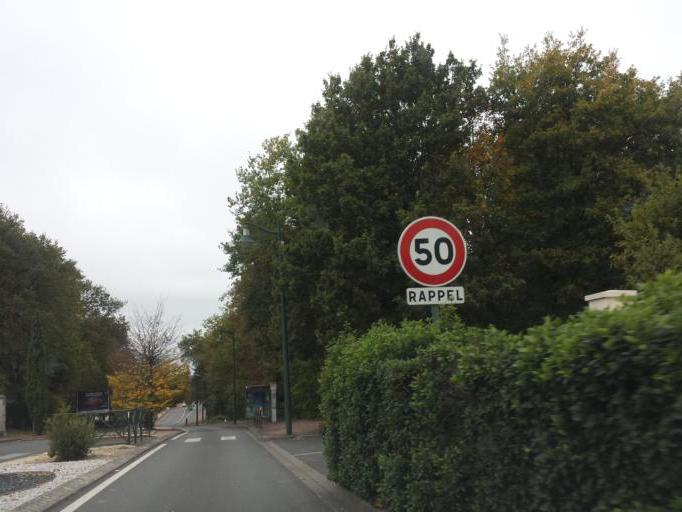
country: FR
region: Poitou-Charentes
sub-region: Departement de la Charente
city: Puymoyen
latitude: 45.6160
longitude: 0.1775
